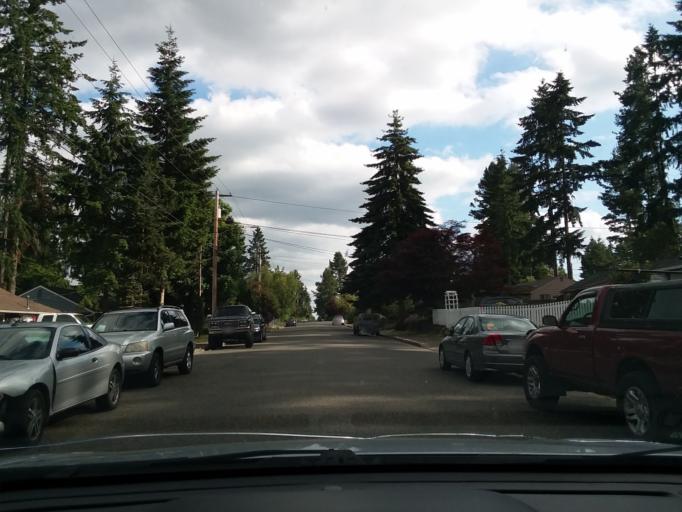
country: US
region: Washington
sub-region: Snohomish County
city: Mountlake Terrace
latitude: 47.7896
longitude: -122.3030
